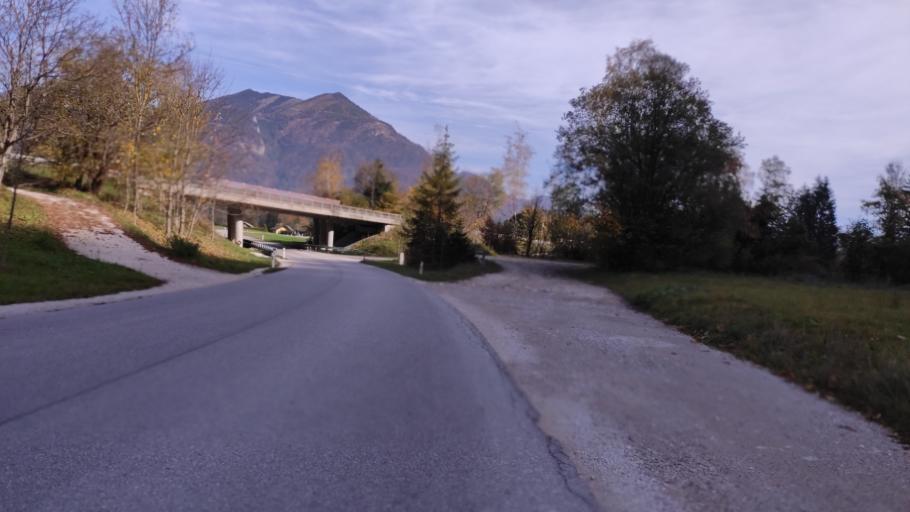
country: AT
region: Salzburg
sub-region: Politischer Bezirk Salzburg-Umgebung
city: Strobl
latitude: 47.7139
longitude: 13.5093
